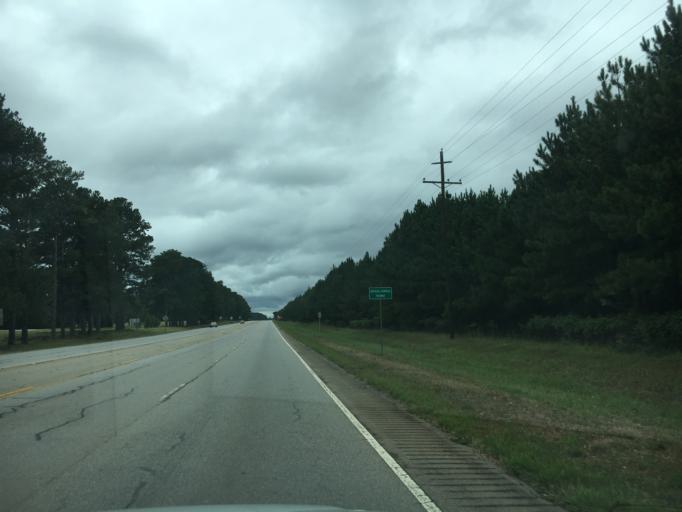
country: US
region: Georgia
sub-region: Wilkes County
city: Washington
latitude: 33.7003
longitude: -82.6898
